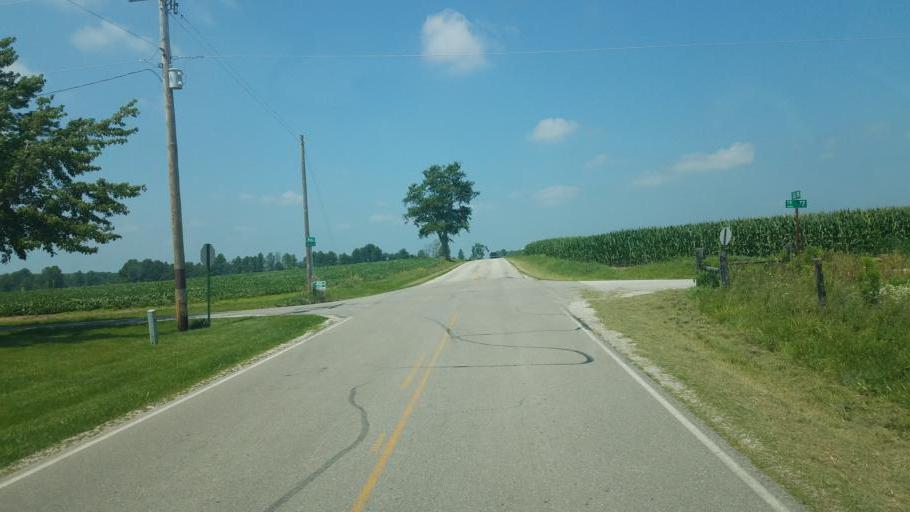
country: US
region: Ohio
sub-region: Crawford County
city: Bucyrus
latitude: 40.9937
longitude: -82.9776
